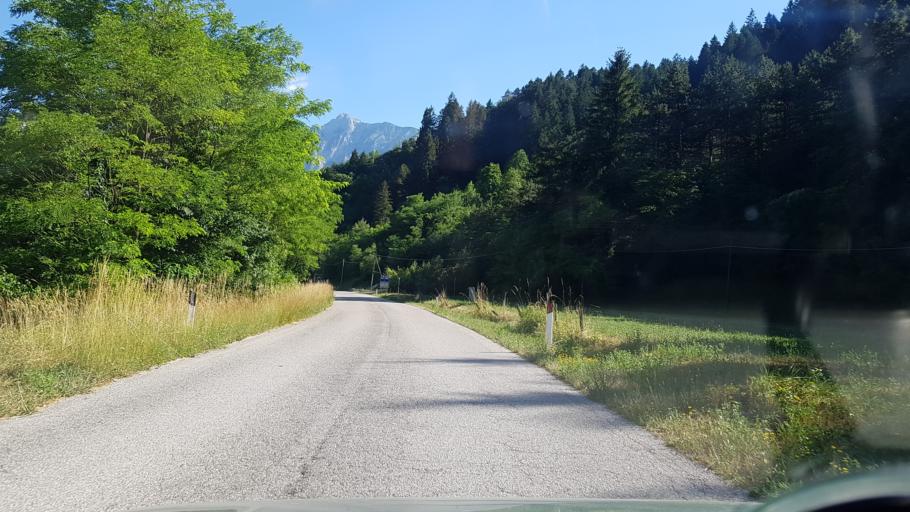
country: IT
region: Friuli Venezia Giulia
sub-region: Provincia di Udine
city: Moggio Udinese
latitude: 46.4193
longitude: 13.1977
